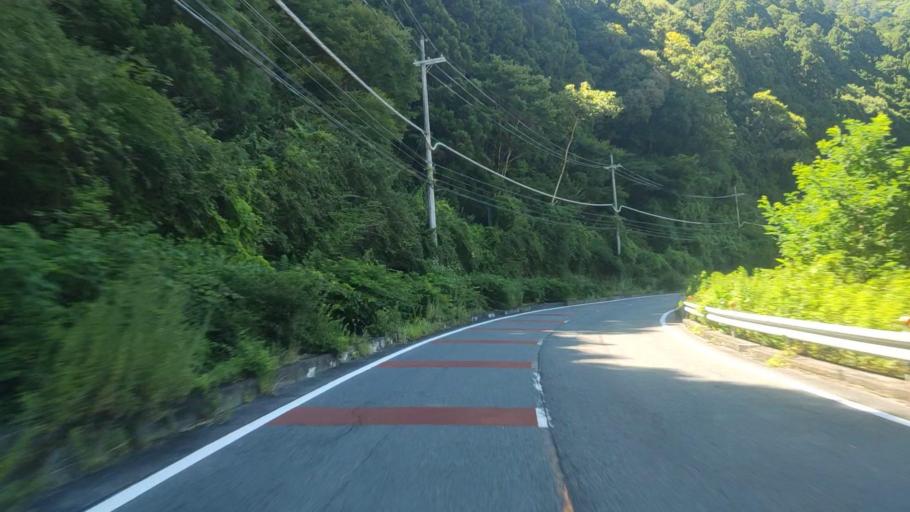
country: JP
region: Nara
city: Yoshino-cho
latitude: 34.3026
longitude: 135.9916
